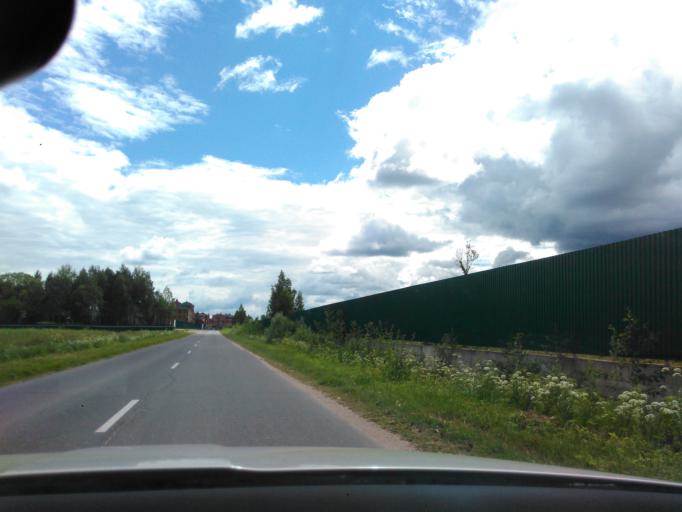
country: RU
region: Tverskaya
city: Konakovo
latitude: 56.6793
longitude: 36.7074
